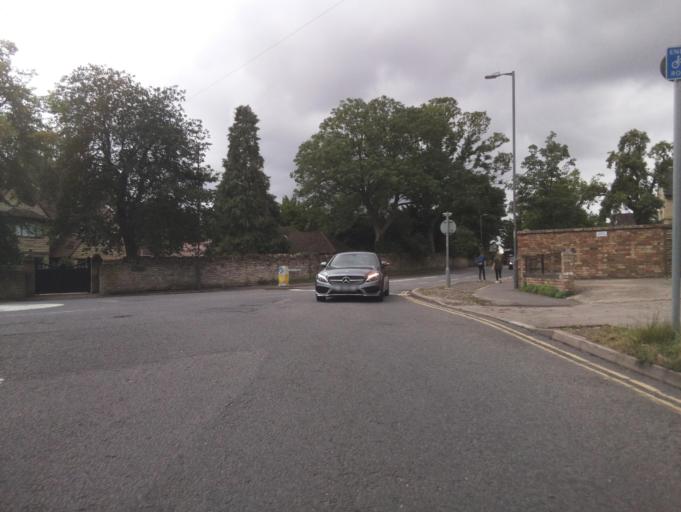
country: GB
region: England
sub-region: Lincolnshire
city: Stamford
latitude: 52.6550
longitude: -0.4705
